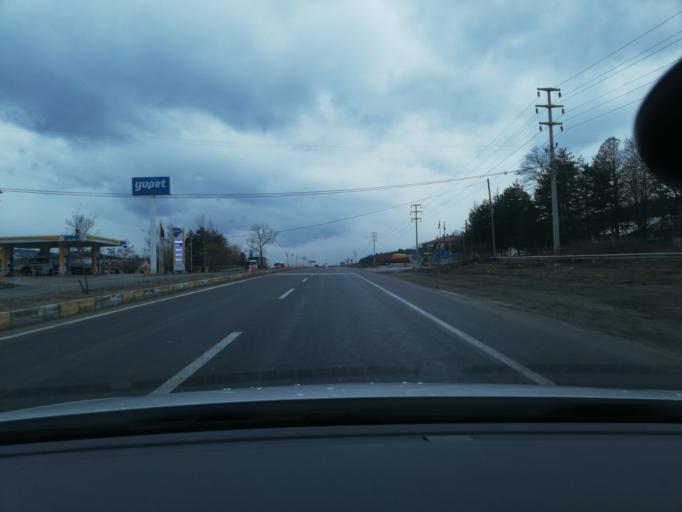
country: TR
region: Bolu
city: Yenicaga
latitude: 40.7576
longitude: 31.9226
